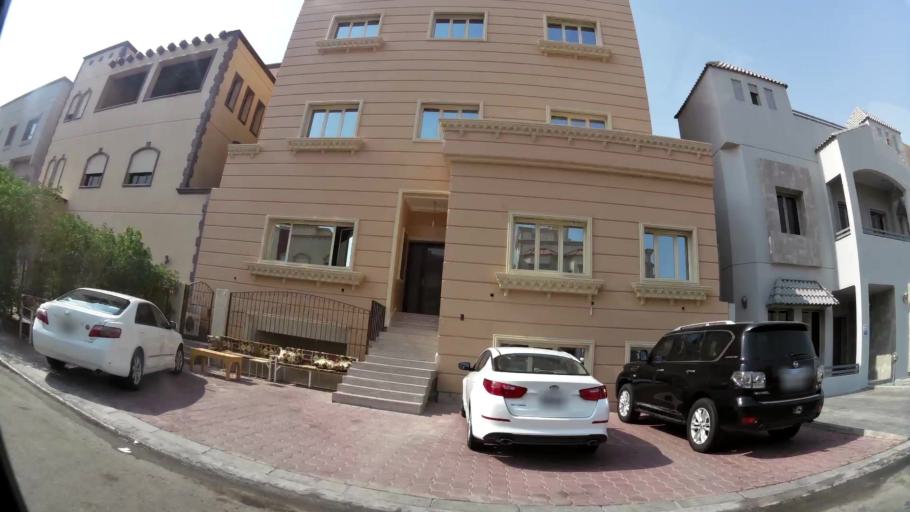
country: KW
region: Muhafazat al Jahra'
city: Al Jahra'
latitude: 29.3321
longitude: 47.7746
